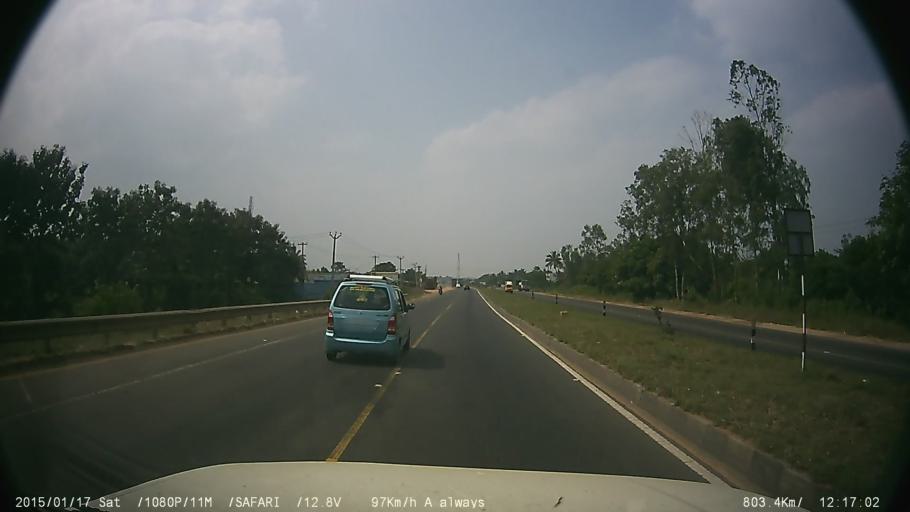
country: IN
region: Tamil Nadu
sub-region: Kancheepuram
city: Sriperumbudur
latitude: 12.9117
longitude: 79.8507
